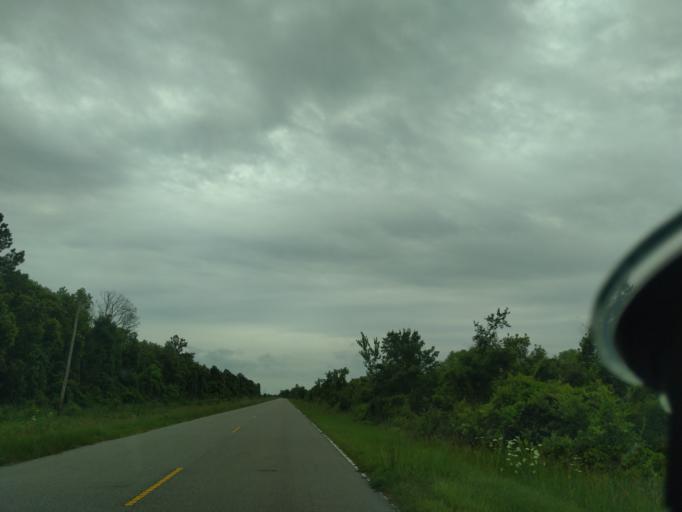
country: US
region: North Carolina
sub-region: Beaufort County
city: Belhaven
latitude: 35.7492
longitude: -76.5038
